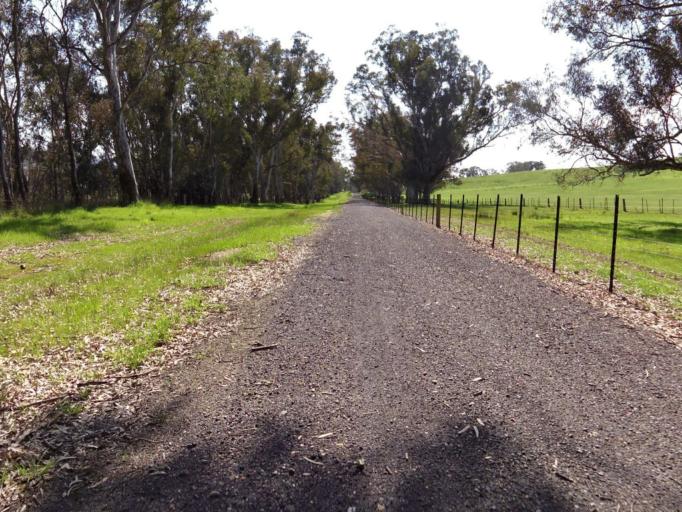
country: AU
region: Victoria
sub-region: Murrindindi
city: Alexandra
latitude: -37.1396
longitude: 145.5903
